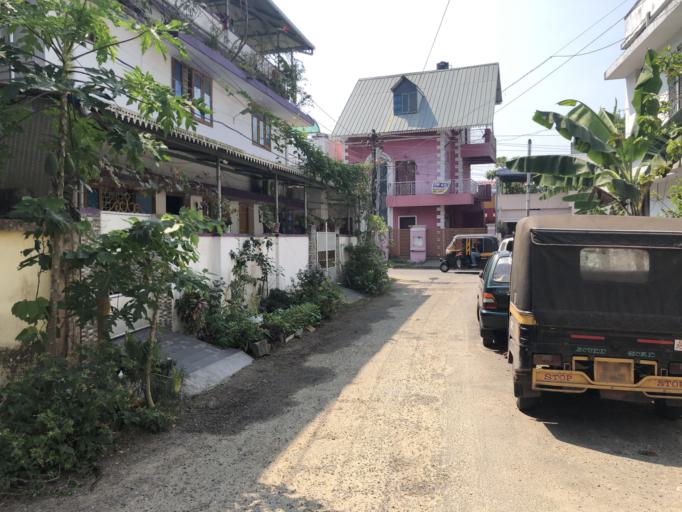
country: IN
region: Kerala
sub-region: Ernakulam
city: Cochin
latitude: 9.9535
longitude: 76.2448
